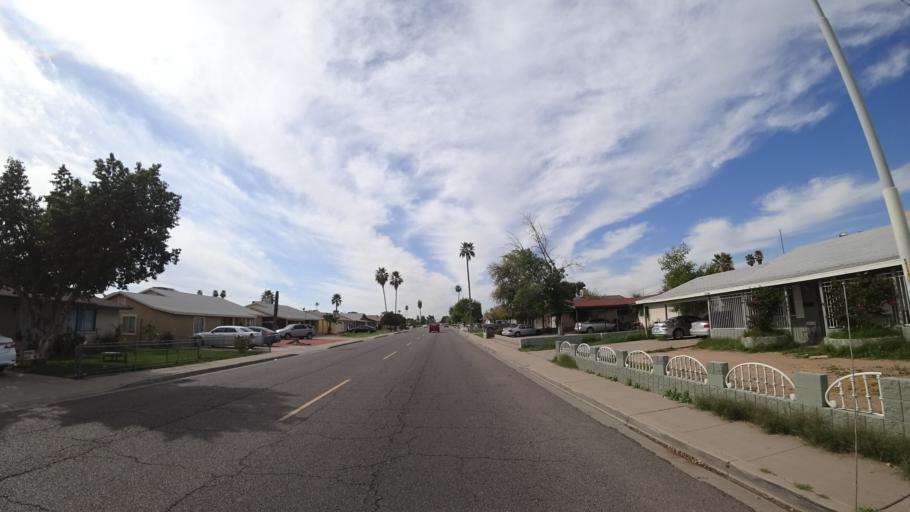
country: US
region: Arizona
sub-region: Maricopa County
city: Glendale
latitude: 33.4733
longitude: -112.1815
